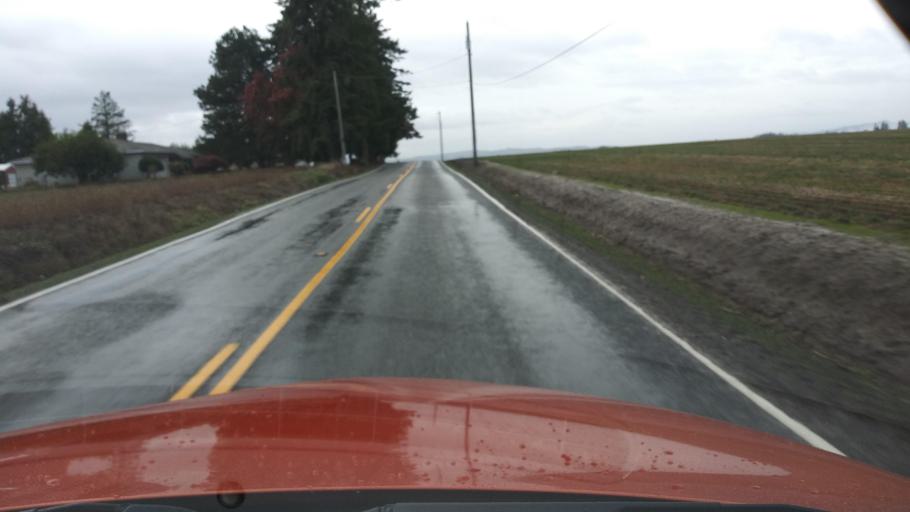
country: US
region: Oregon
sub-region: Washington County
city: North Plains
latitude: 45.5855
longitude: -123.0175
